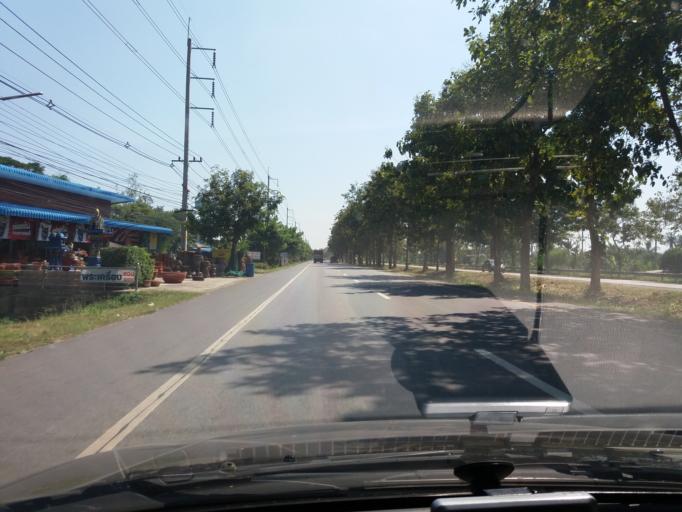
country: TH
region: Chai Nat
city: Sankhaburi
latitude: 15.0899
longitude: 100.1391
